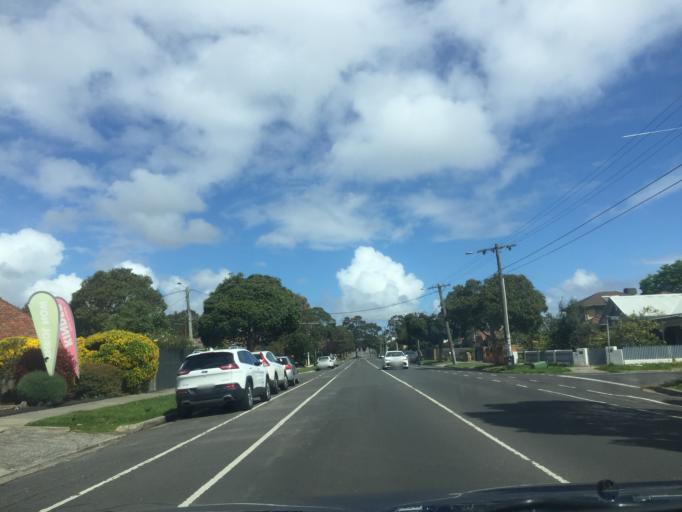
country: AU
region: Victoria
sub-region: Darebin
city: Preston
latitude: -37.7483
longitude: 145.0166
